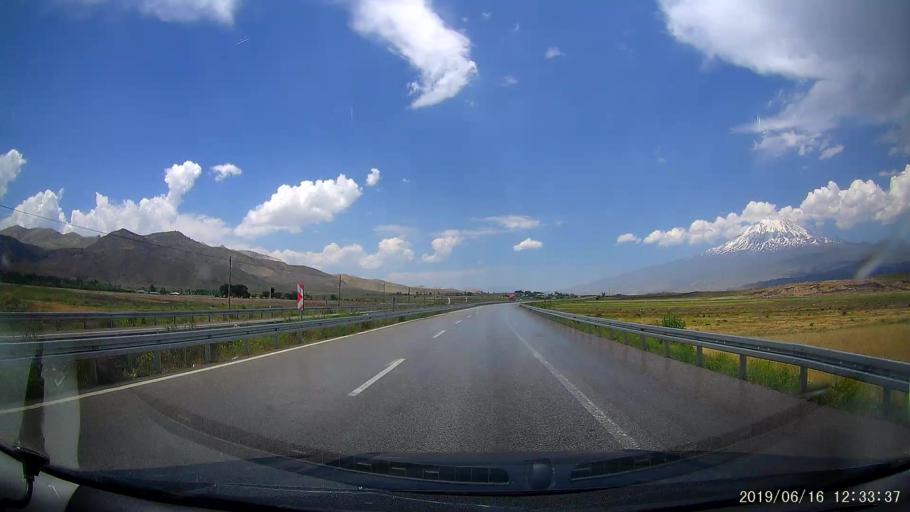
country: TR
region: Agri
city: Dogubayazit
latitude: 39.4676
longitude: 44.2611
